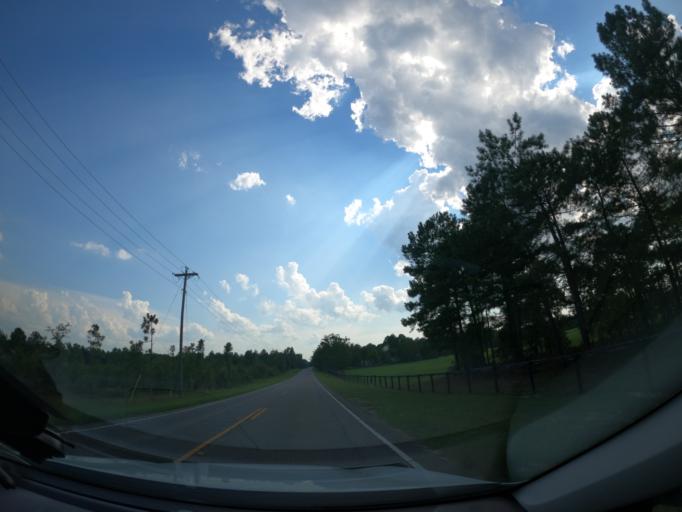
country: US
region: South Carolina
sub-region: Barnwell County
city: Williston
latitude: 33.5063
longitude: -81.5066
